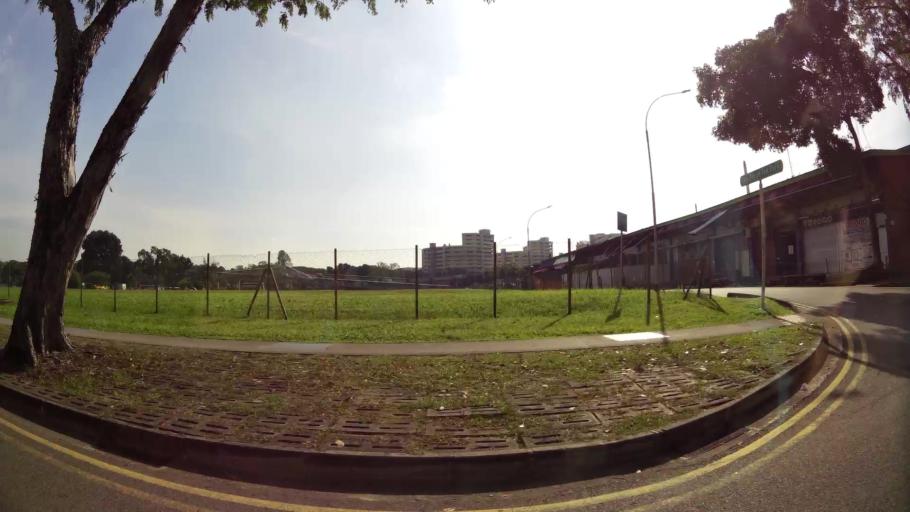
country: SG
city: Singapore
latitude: 1.3375
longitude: 103.8599
